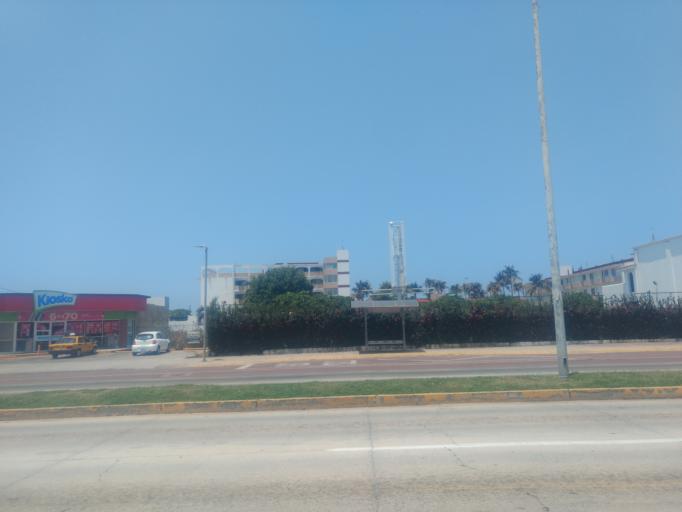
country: MX
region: Colima
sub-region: Manzanillo
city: Manzanillo
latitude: 19.0990
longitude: -104.3234
